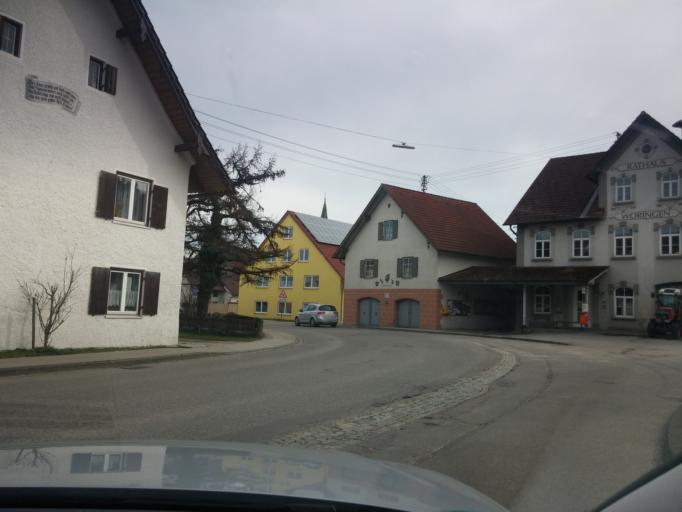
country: DE
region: Bavaria
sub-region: Swabia
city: Woringen
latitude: 47.9236
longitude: 10.2010
